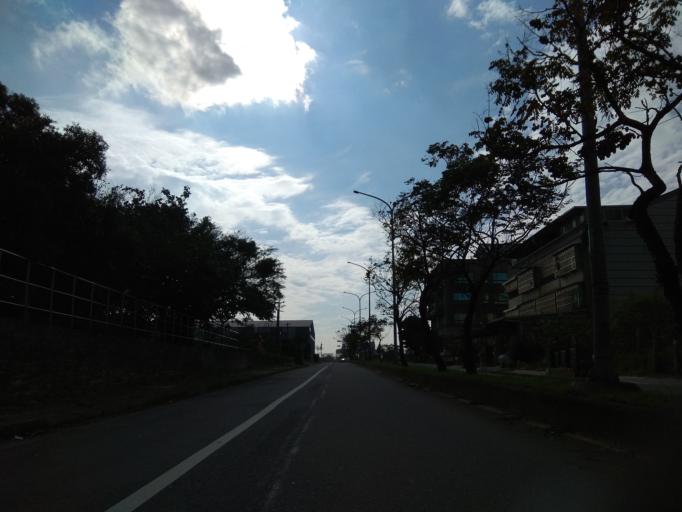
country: TW
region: Taiwan
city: Taoyuan City
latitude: 25.0511
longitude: 121.1772
